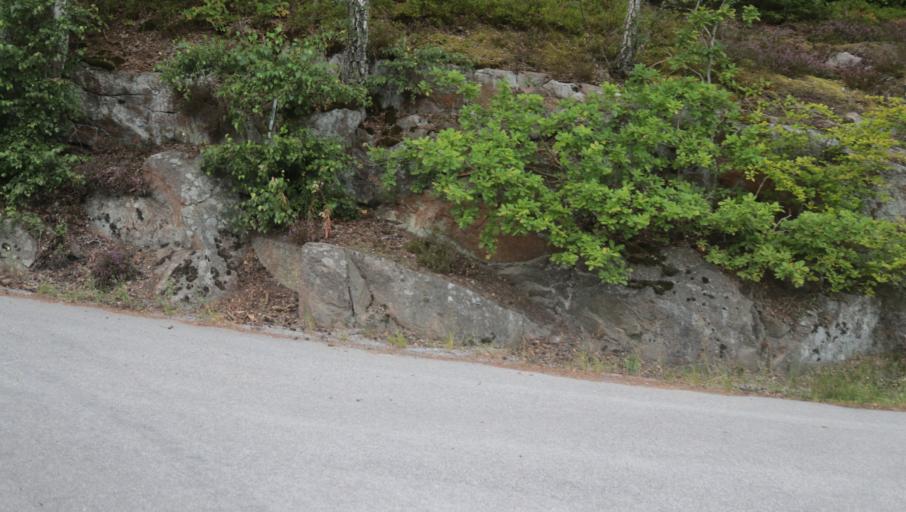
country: SE
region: Blekinge
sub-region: Karlshamns Kommun
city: Karlshamn
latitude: 56.2073
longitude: 14.8713
